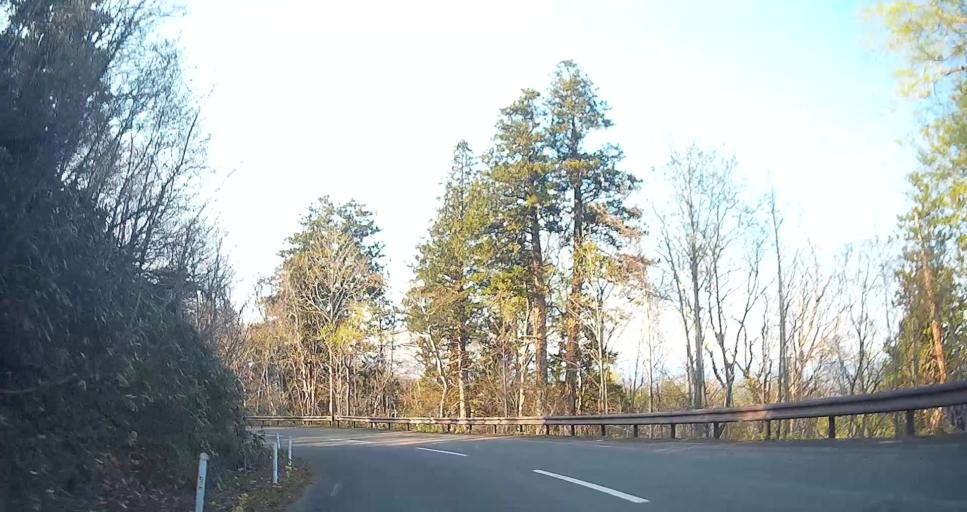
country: JP
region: Aomori
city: Mutsu
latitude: 41.3143
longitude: 141.1096
